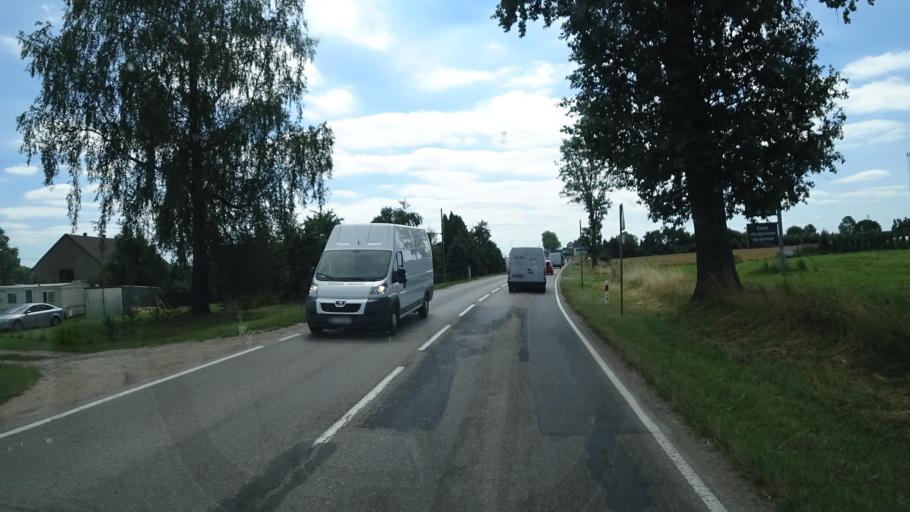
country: PL
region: Warmian-Masurian Voivodeship
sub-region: Powiat elcki
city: Elk
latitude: 53.7619
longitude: 22.3377
